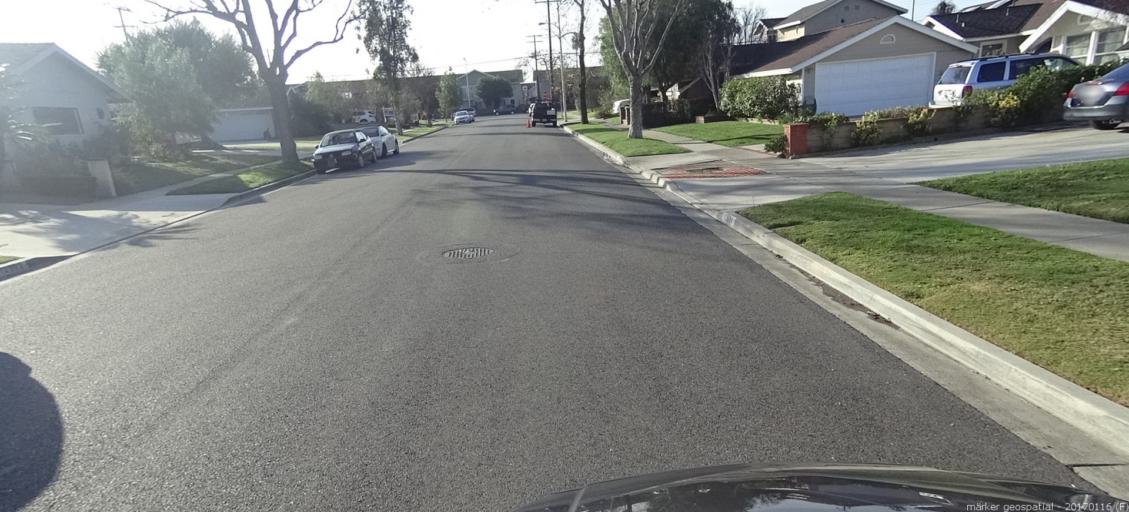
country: US
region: California
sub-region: Orange County
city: Rossmoor
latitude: 33.7887
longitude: -118.0735
